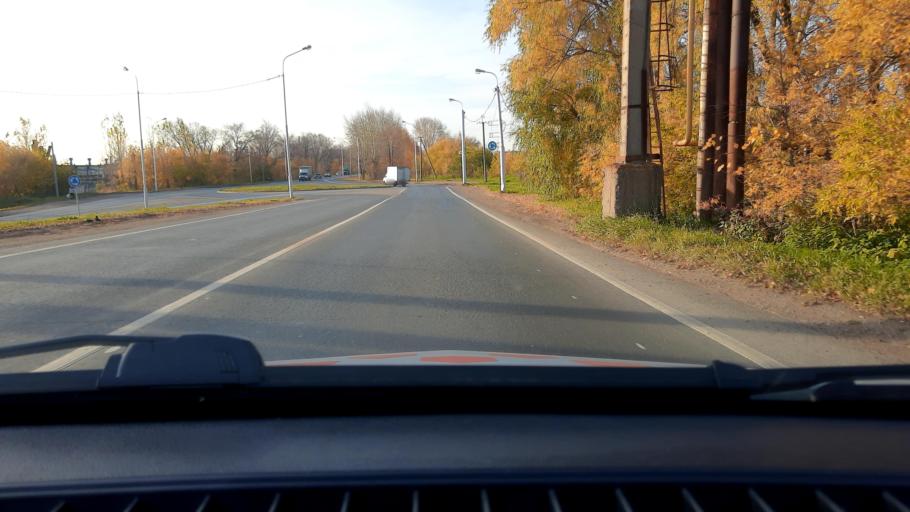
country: RU
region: Bashkortostan
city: Blagoveshchensk
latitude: 54.9134
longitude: 56.0815
